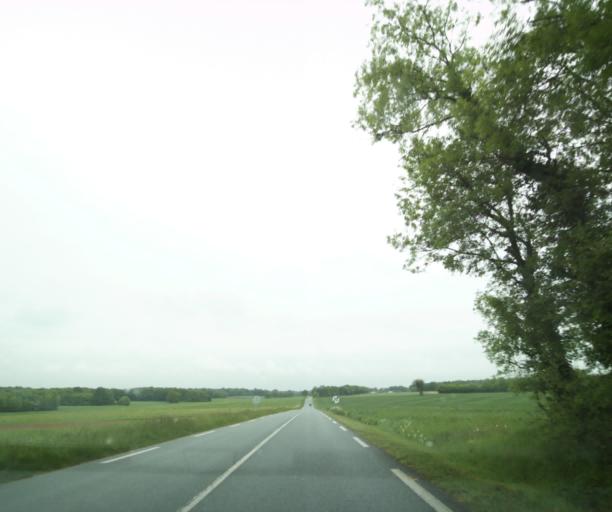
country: FR
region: Poitou-Charentes
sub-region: Departement de la Charente-Maritime
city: Nieul-les-Saintes
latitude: 45.7452
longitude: -0.7160
